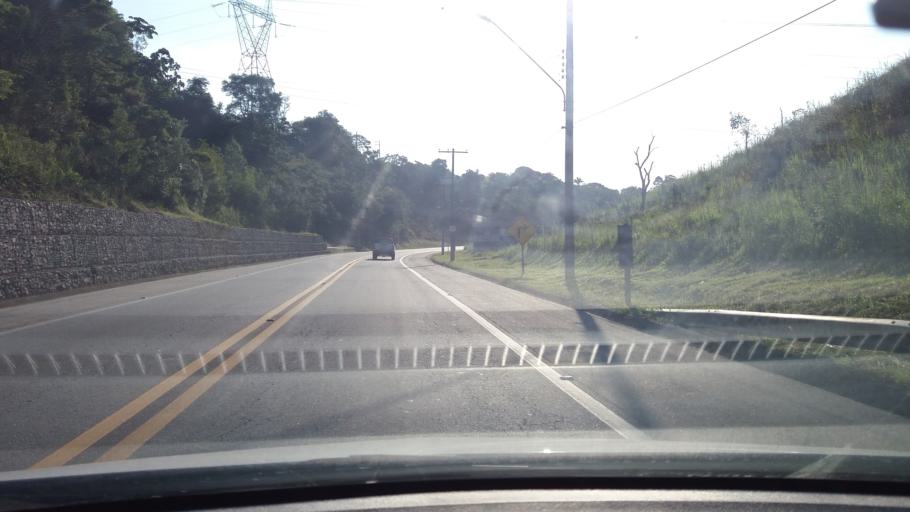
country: BR
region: Sao Paulo
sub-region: Mairipora
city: Mairipora
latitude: -23.3276
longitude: -46.6014
